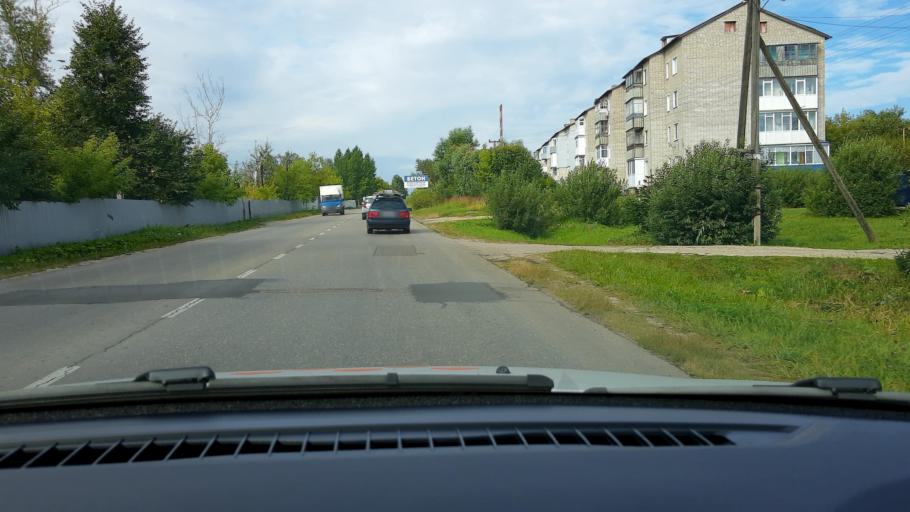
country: RU
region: Nizjnij Novgorod
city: Arzamas
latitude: 55.4197
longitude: 43.8506
